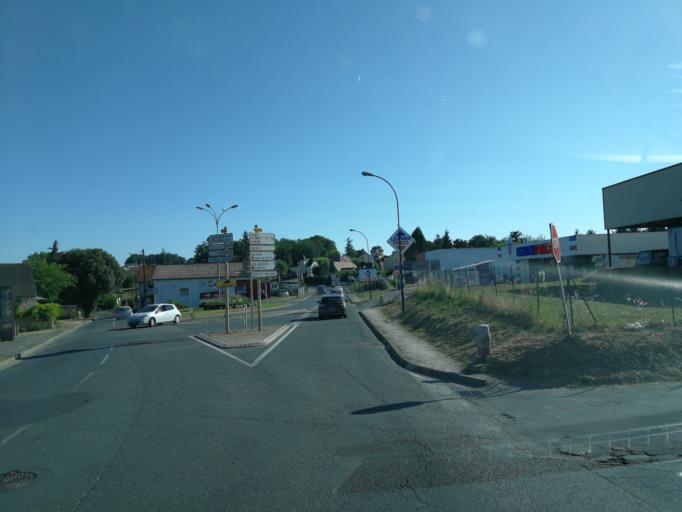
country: FR
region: Midi-Pyrenees
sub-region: Departement du Lot
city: Gourdon
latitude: 44.7322
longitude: 1.3753
